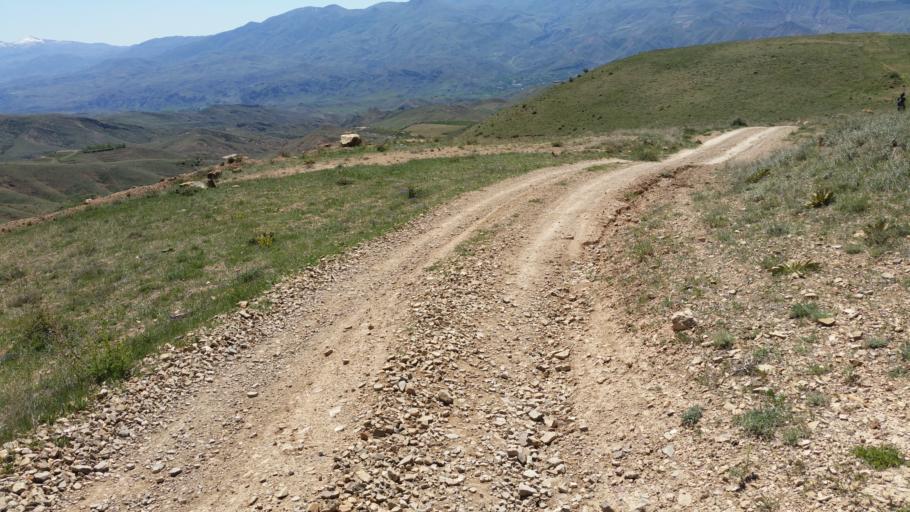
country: AM
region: Vayots' Dzori Marz
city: Vernashen
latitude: 39.8007
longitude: 45.3608
